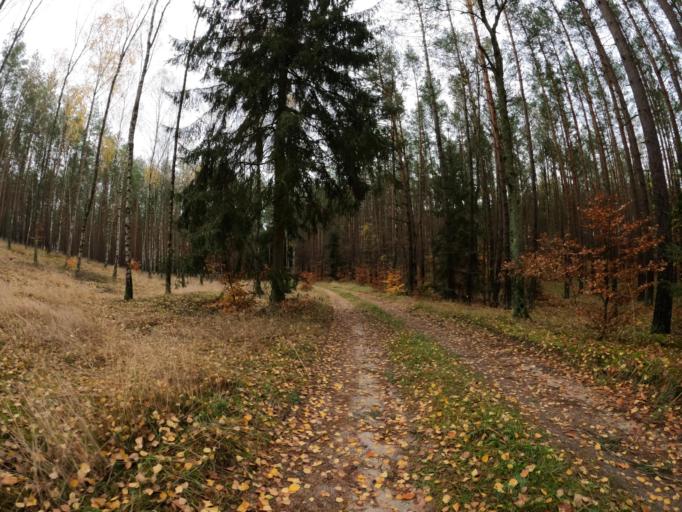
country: PL
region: West Pomeranian Voivodeship
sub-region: Powiat walecki
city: Miroslawiec
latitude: 53.3229
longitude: 16.1097
